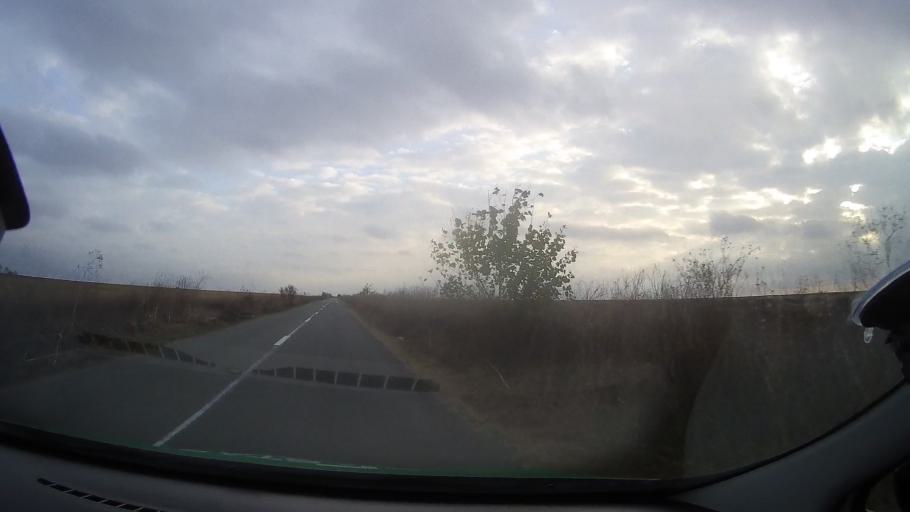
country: RO
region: Constanta
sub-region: Comuna Pestera
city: Pestera
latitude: 44.1405
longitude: 28.1171
